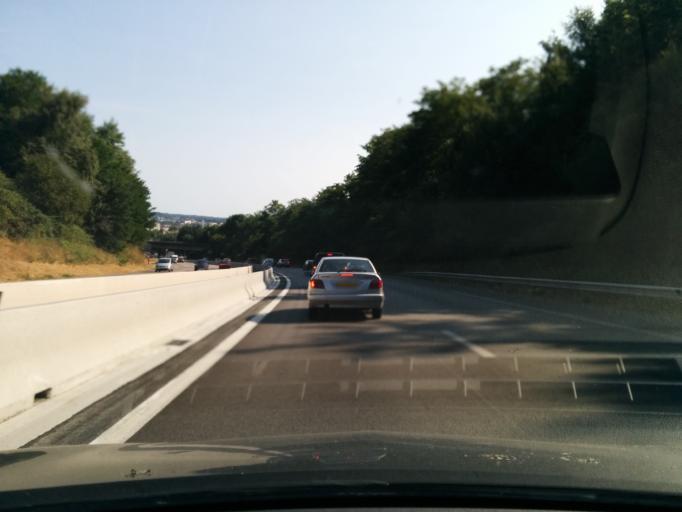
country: FR
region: Limousin
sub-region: Departement de la Haute-Vienne
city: Limoges
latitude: 45.8531
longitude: 1.2761
